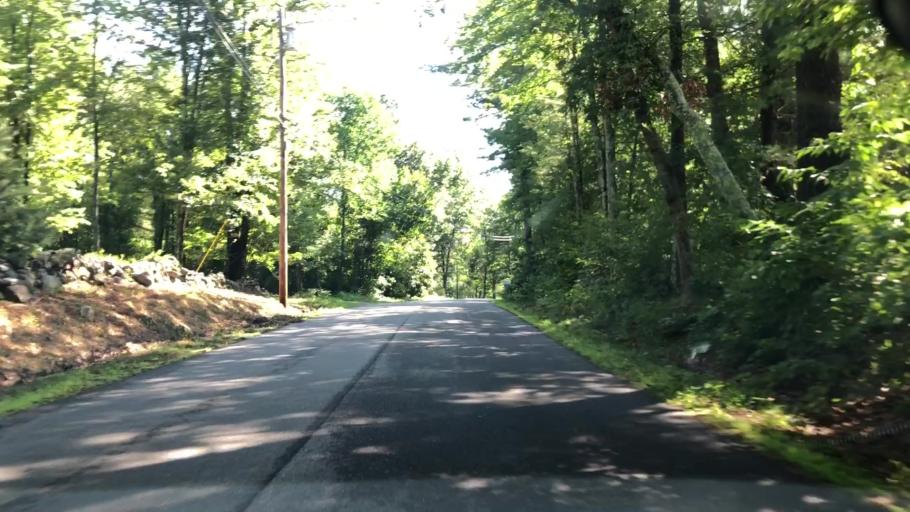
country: US
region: New Hampshire
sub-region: Hillsborough County
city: Milford
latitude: 42.8425
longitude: -71.5920
